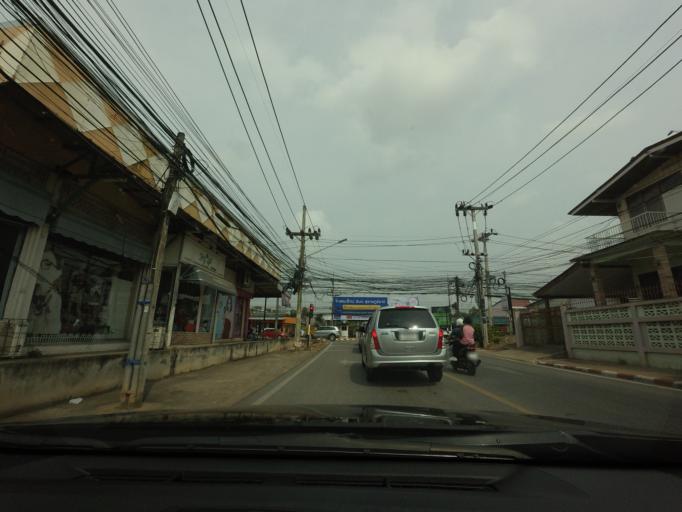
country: TH
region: Surat Thani
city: Surat Thani
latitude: 9.1077
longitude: 99.3072
